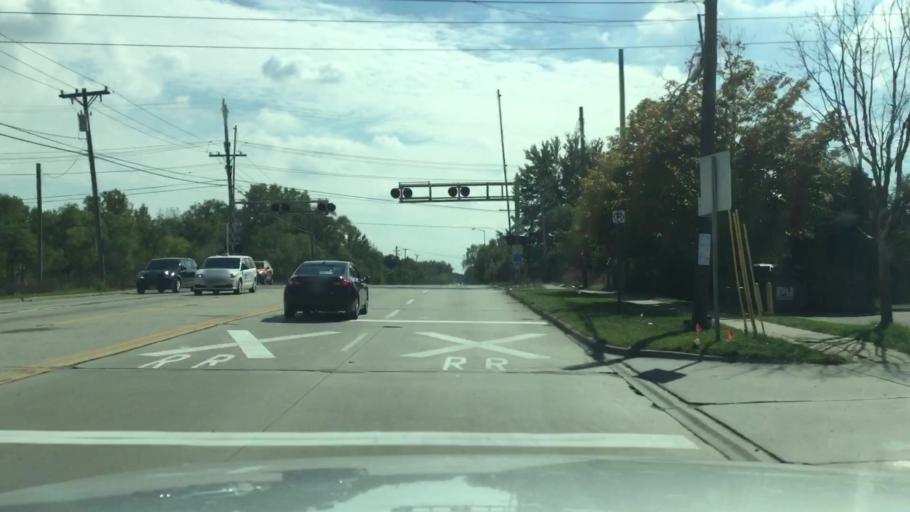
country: US
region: Michigan
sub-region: Wayne County
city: Wayne
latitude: 42.2850
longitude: -83.3488
